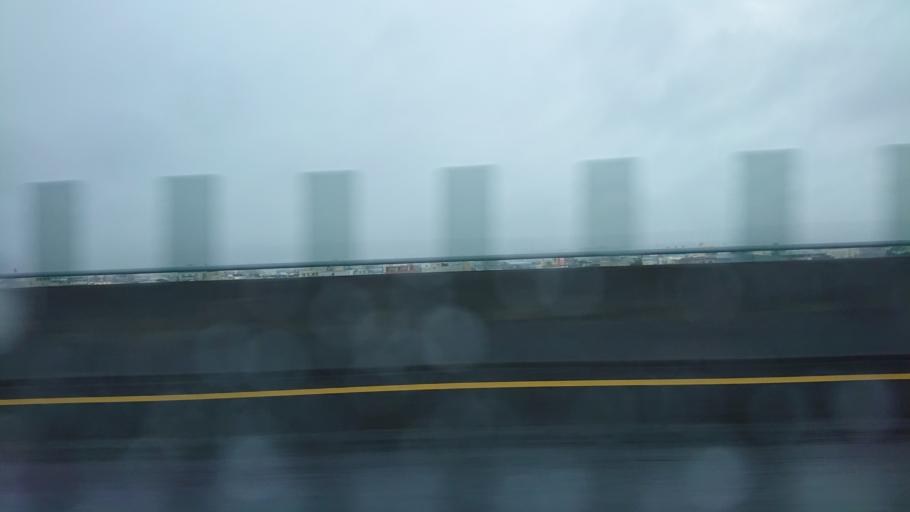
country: TW
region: Taiwan
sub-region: Changhua
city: Chang-hua
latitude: 24.2235
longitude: 120.5250
